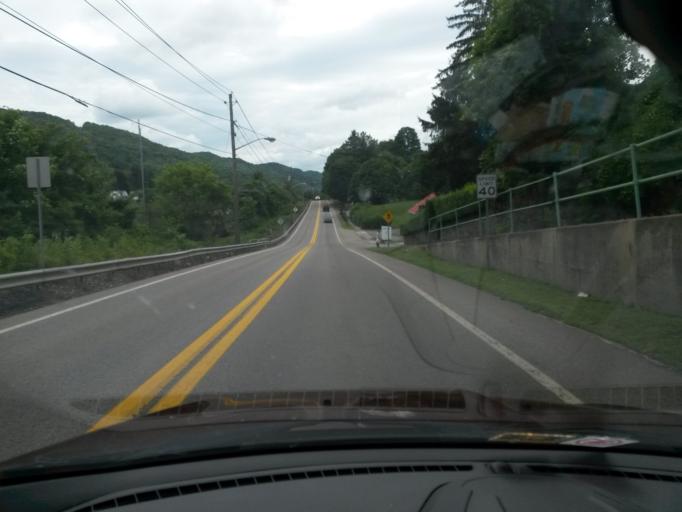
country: US
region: West Virginia
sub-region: Mercer County
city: Bluefield
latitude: 37.2717
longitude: -81.2168
